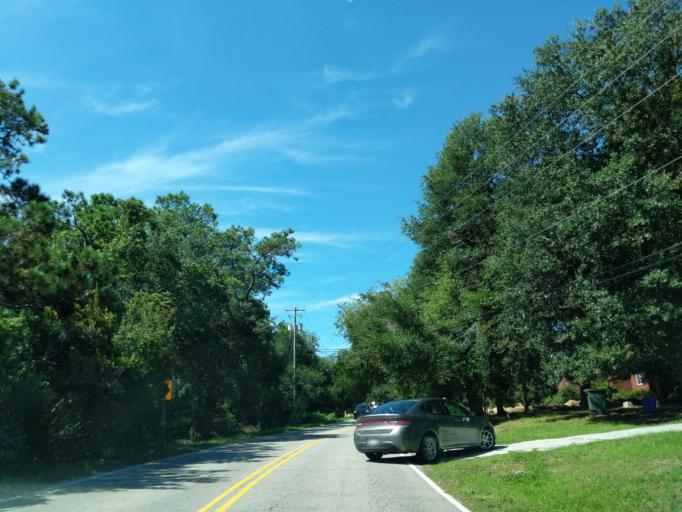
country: US
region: South Carolina
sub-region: Charleston County
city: Folly Beach
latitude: 32.7036
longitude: -79.9575
